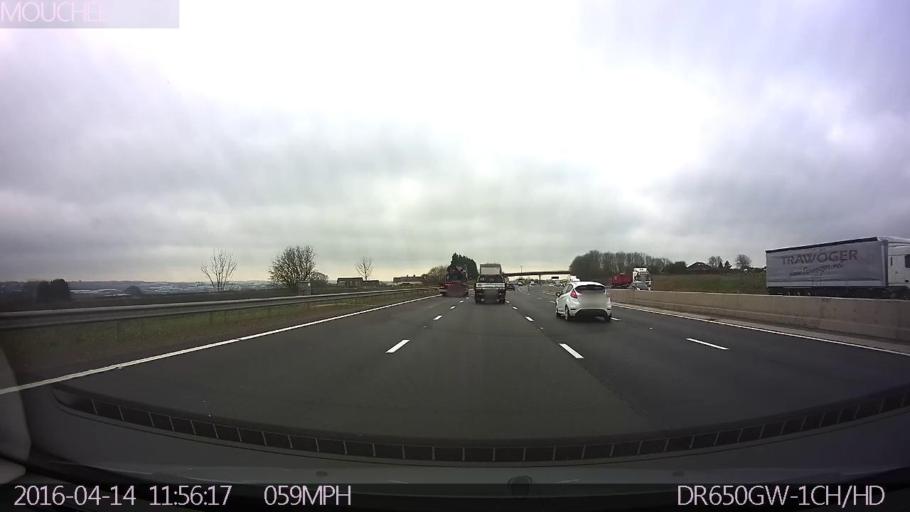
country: GB
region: England
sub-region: Derbyshire
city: Blackwell
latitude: 53.1325
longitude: -1.3290
